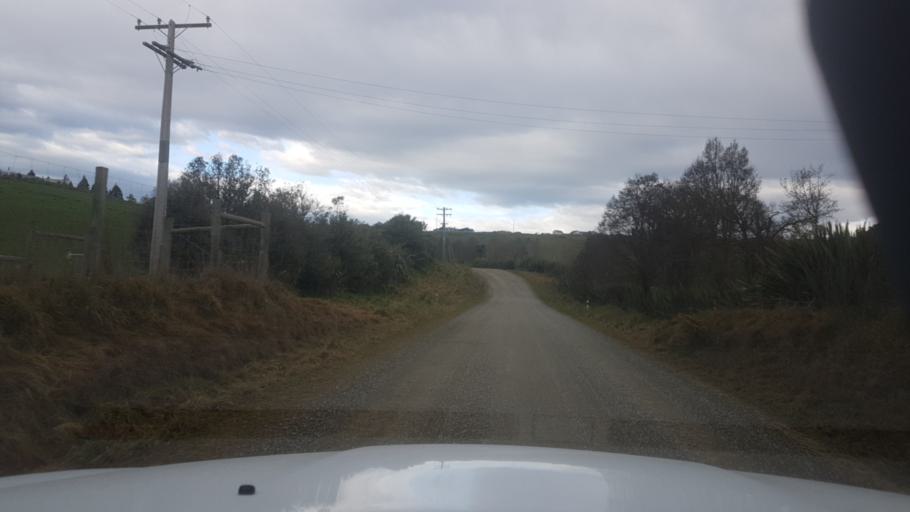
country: NZ
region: Canterbury
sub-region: Timaru District
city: Pleasant Point
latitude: -44.3473
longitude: 171.1570
